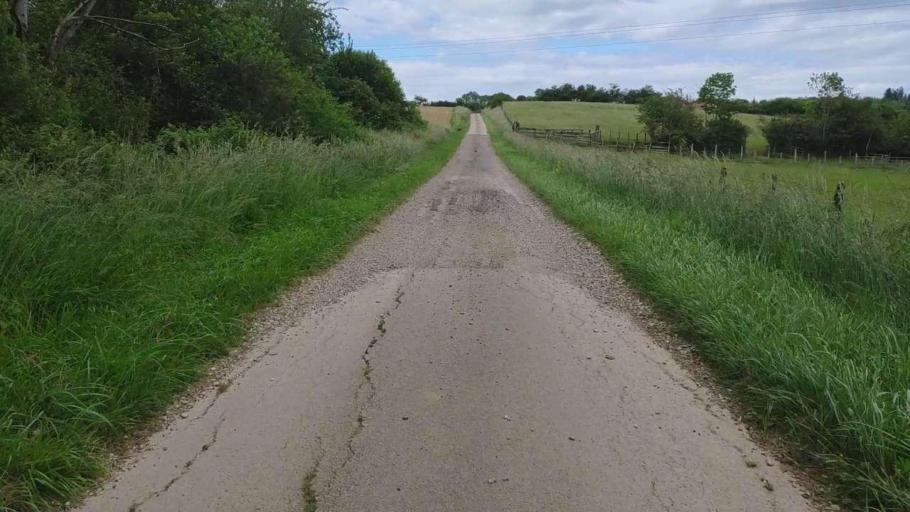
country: FR
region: Franche-Comte
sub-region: Departement du Jura
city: Bletterans
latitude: 46.7894
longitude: 5.5507
